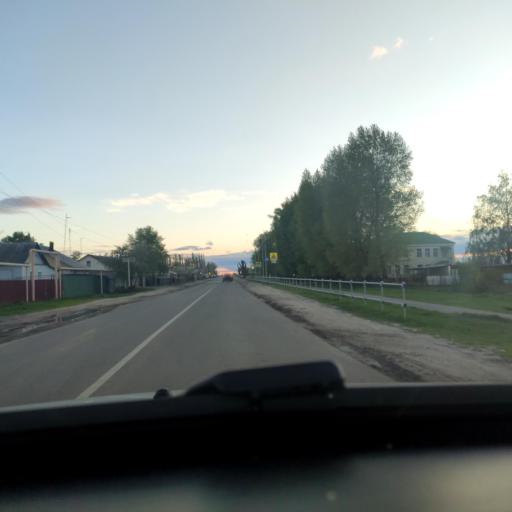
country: RU
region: Voronezj
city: Novovoronezh
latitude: 51.3495
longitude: 39.2947
